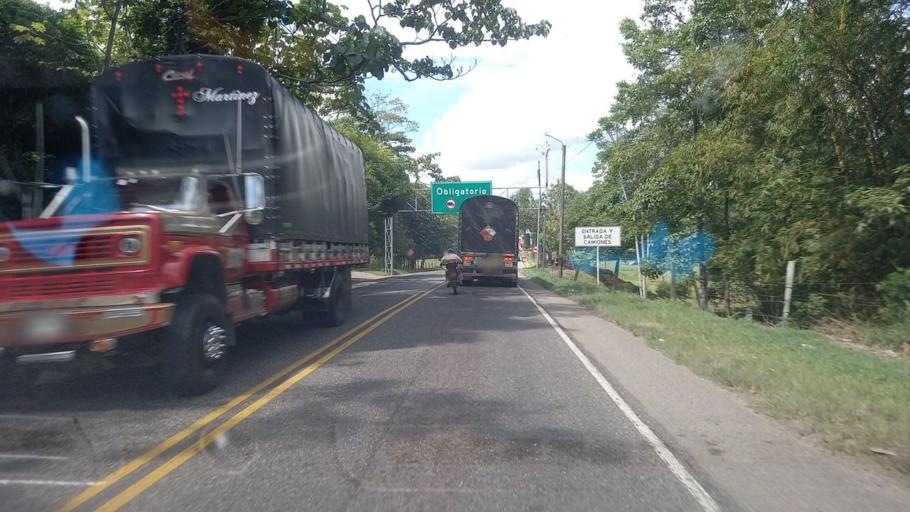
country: CO
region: Santander
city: Sabana de Torres
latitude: 7.1263
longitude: -73.5780
